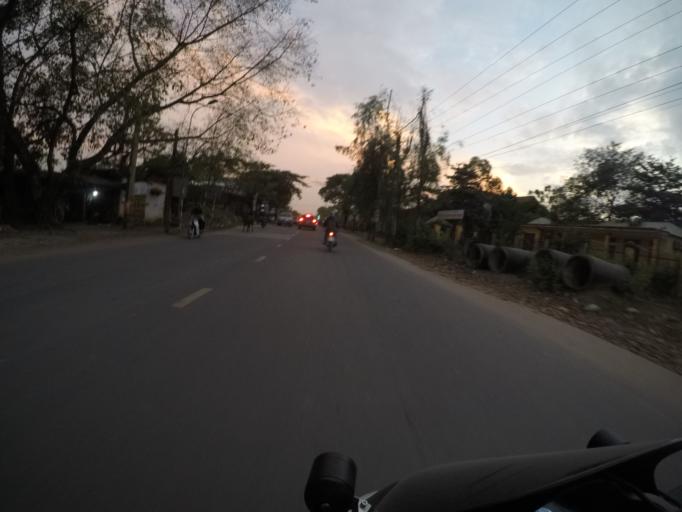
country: VN
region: Vinh Phuc
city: Phuc Yen
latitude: 21.2728
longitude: 105.7245
